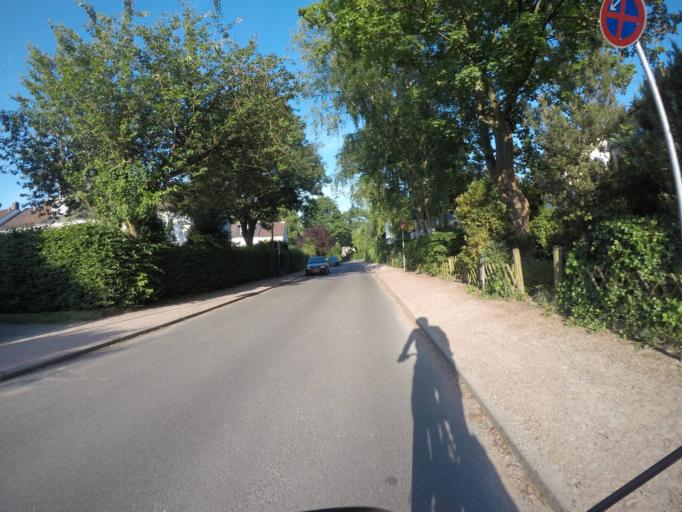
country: DE
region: Schleswig-Holstein
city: Rellingen
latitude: 53.5796
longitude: 9.7900
